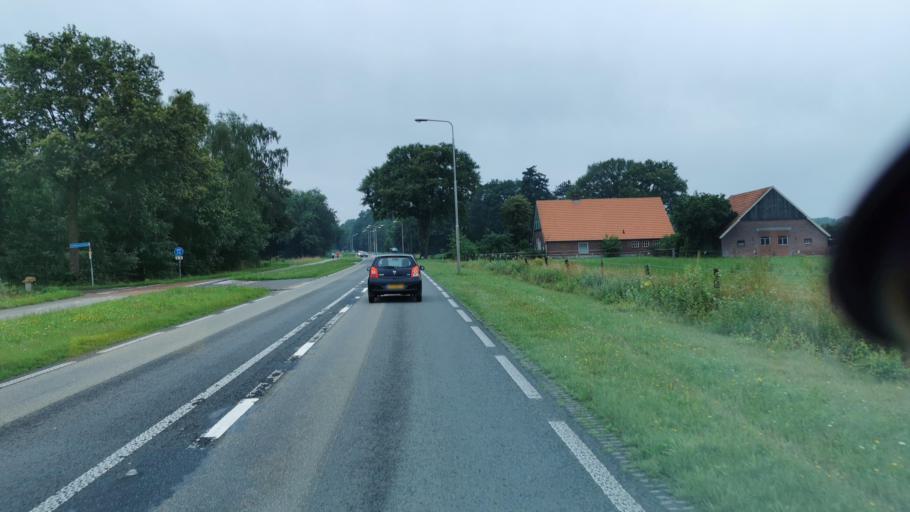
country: NL
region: Overijssel
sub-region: Gemeente Oldenzaal
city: Oldenzaal
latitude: 52.2835
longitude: 6.9611
